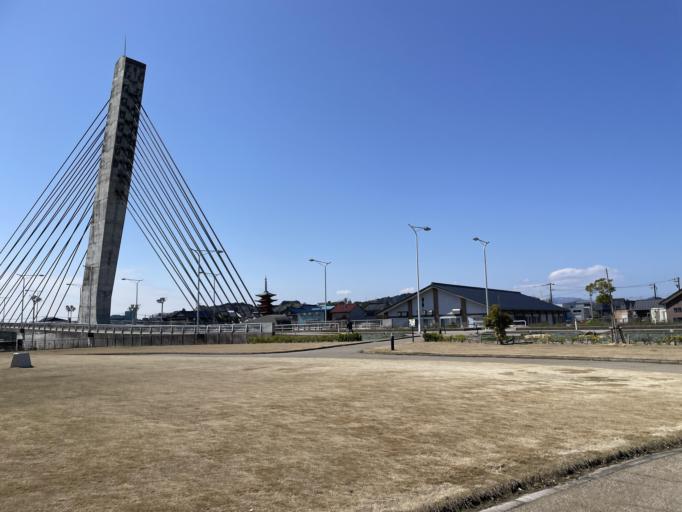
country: JP
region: Toyama
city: Himi
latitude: 36.8641
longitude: 136.9884
